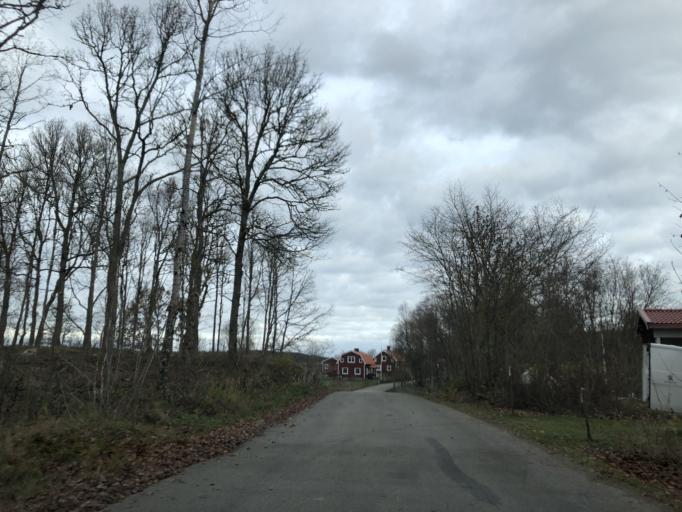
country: SE
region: Vaestra Goetaland
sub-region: Ulricehamns Kommun
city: Ulricehamn
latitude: 57.7167
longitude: 13.3585
